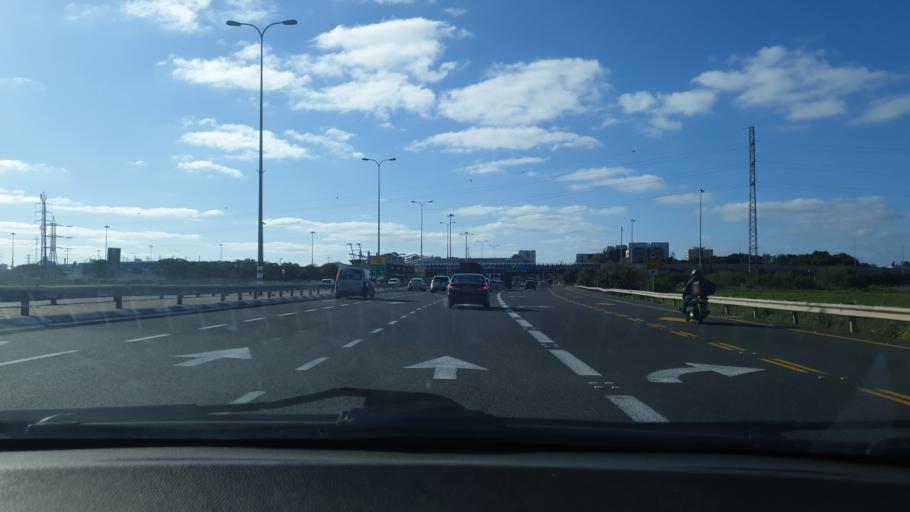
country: IL
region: Tel Aviv
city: Holon
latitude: 32.0370
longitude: 34.7815
